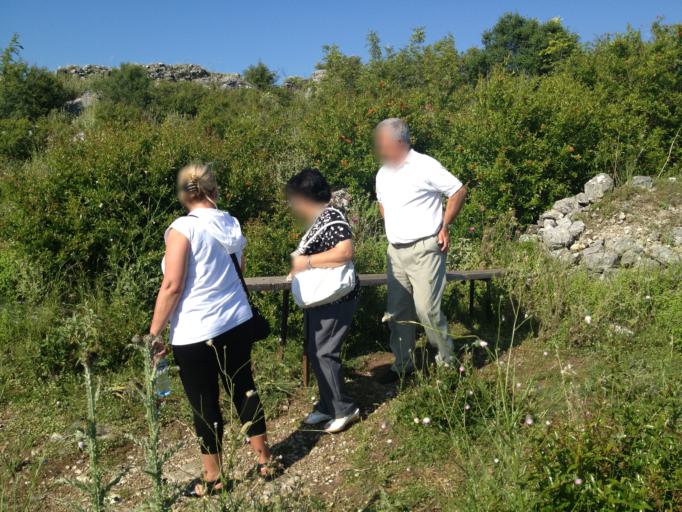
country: AL
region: Shkoder
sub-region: Rrethi i Shkodres
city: Dajc
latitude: 41.9860
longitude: 19.3163
